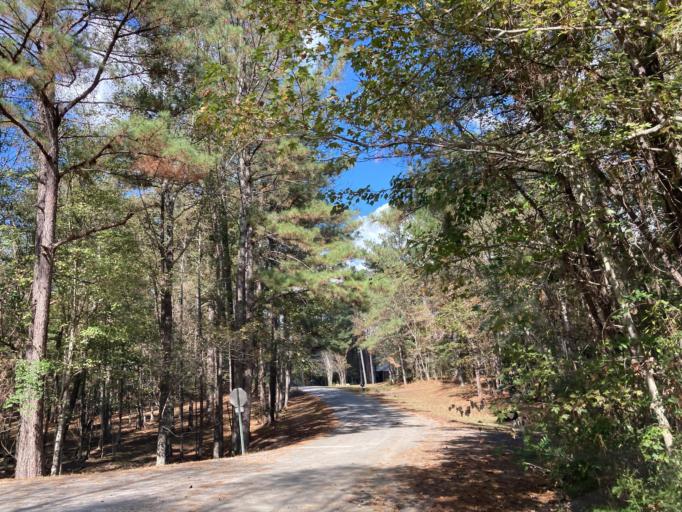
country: US
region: Mississippi
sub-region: Lamar County
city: West Hattiesburg
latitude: 31.2699
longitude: -89.4001
